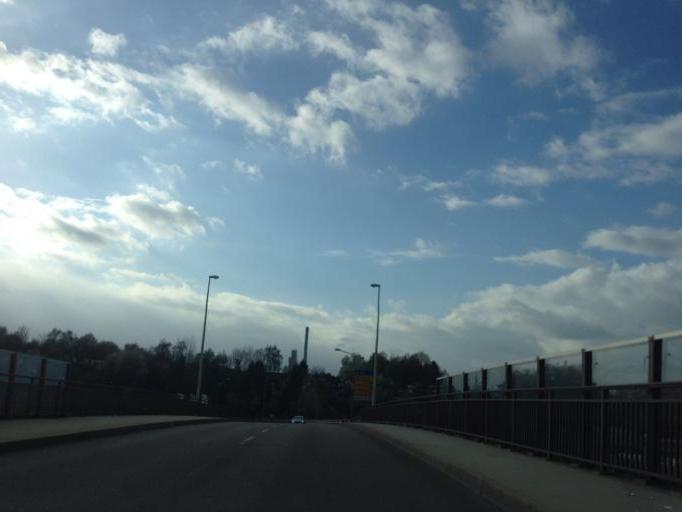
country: DE
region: Saxony
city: Freital
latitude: 51.0097
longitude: 13.6566
